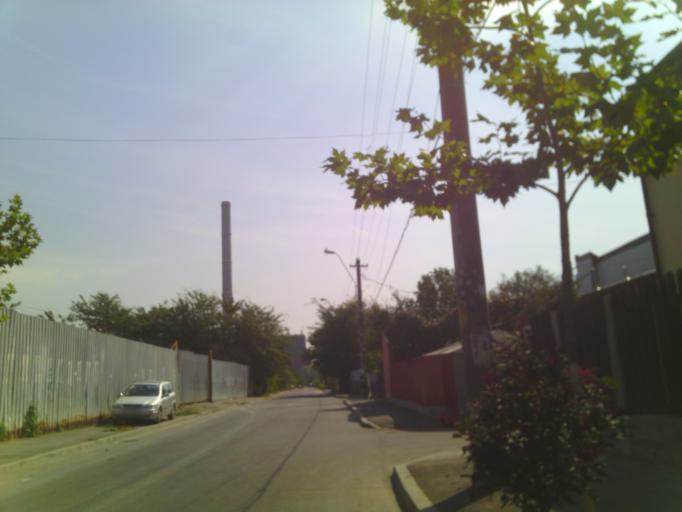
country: RO
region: Ilfov
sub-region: Comuna Jilava
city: Jilava
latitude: 44.3723
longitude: 26.0975
